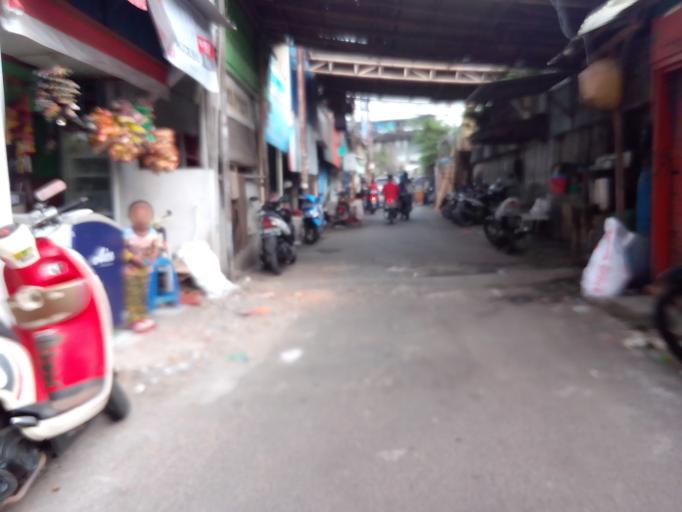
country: ID
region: Jakarta Raya
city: Jakarta
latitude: -6.1653
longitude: 106.8004
